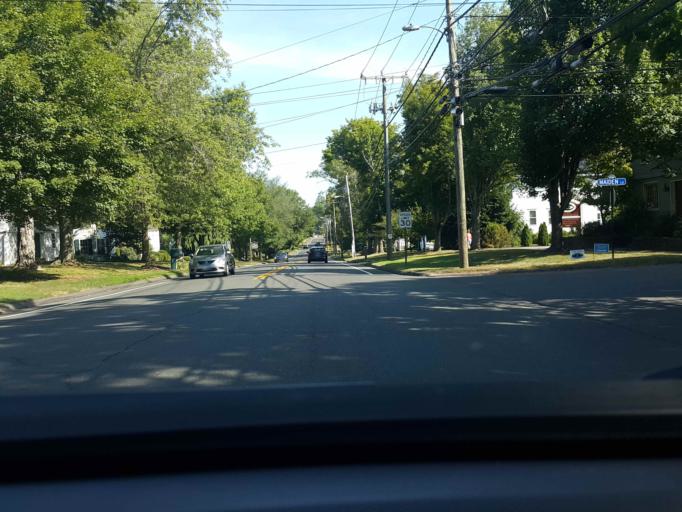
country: US
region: Connecticut
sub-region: Middlesex County
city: Durham
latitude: 41.4788
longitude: -72.6813
